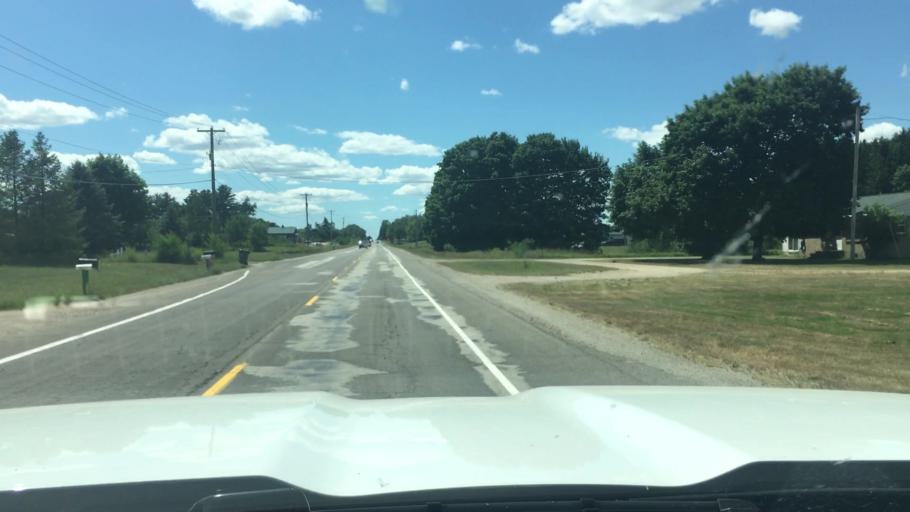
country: US
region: Michigan
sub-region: Kent County
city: Rockford
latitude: 43.1607
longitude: -85.6189
